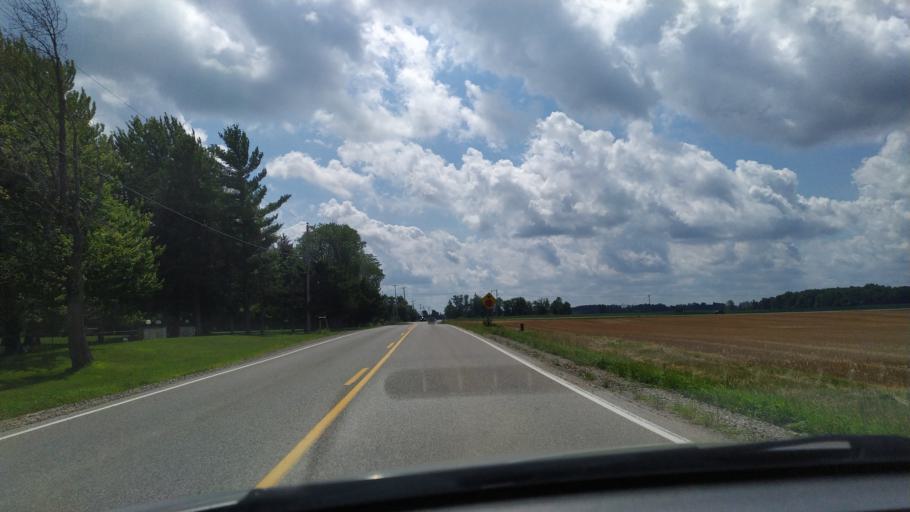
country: CA
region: Ontario
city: London
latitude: 43.0446
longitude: -81.3240
